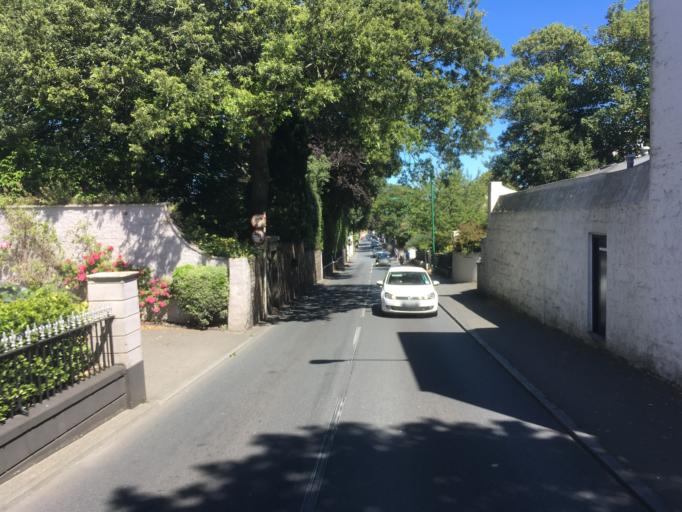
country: GG
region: St Peter Port
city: Saint Peter Port
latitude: 49.4559
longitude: -2.5452
